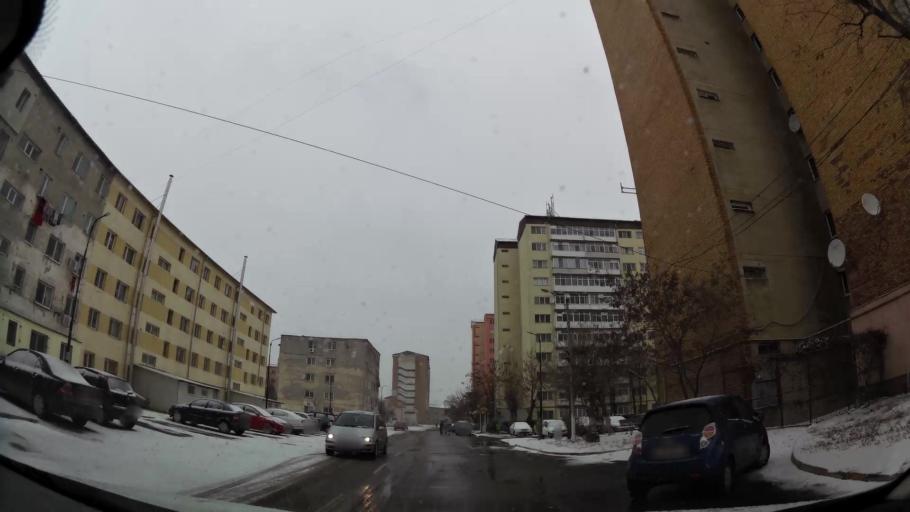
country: RO
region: Dambovita
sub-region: Municipiul Targoviste
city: Targoviste
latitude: 44.9205
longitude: 25.4744
